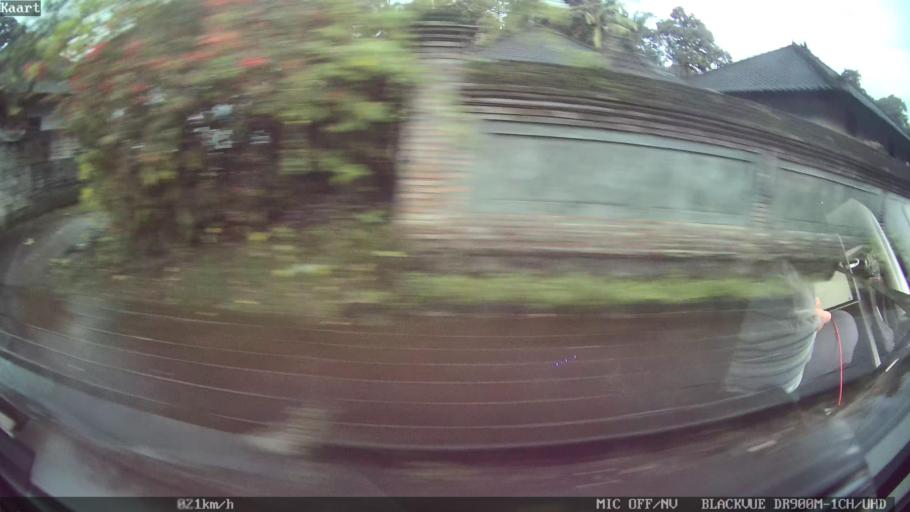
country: ID
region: Bali
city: Banjar Teguan
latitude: -8.5035
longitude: 115.2313
